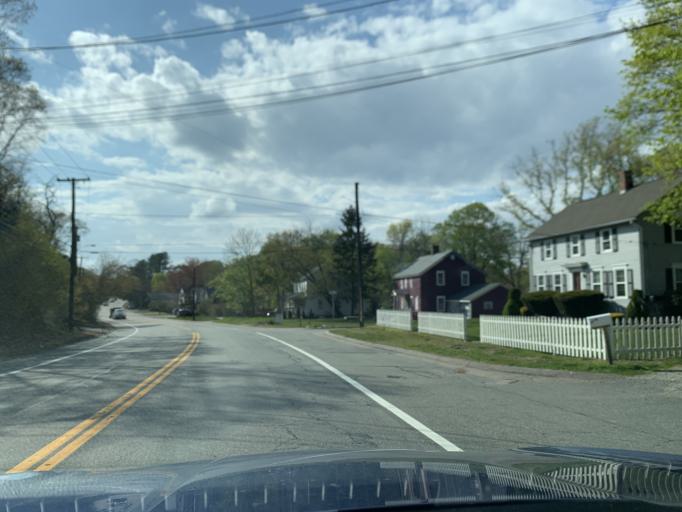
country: US
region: Rhode Island
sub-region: Washington County
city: North Kingstown
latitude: 41.5715
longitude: -71.4796
